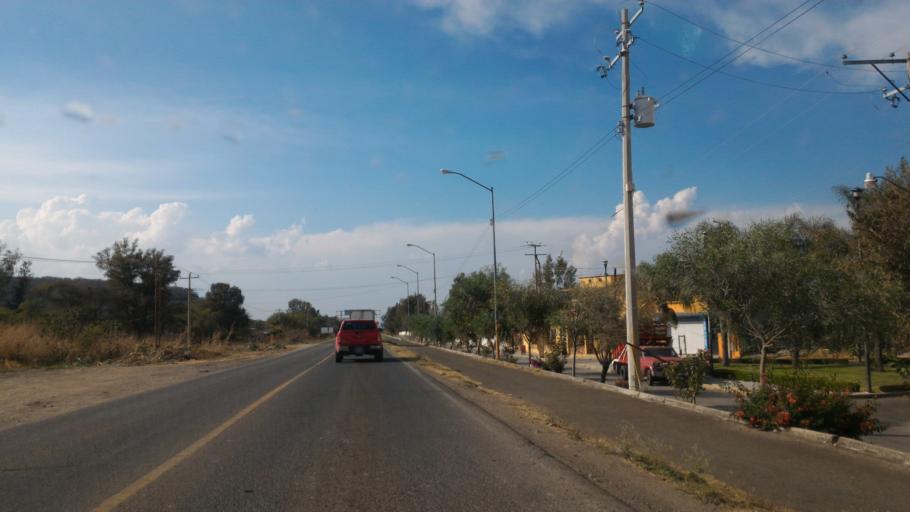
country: MX
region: Guanajuato
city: Ciudad Manuel Doblado
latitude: 20.7424
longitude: -101.9568
